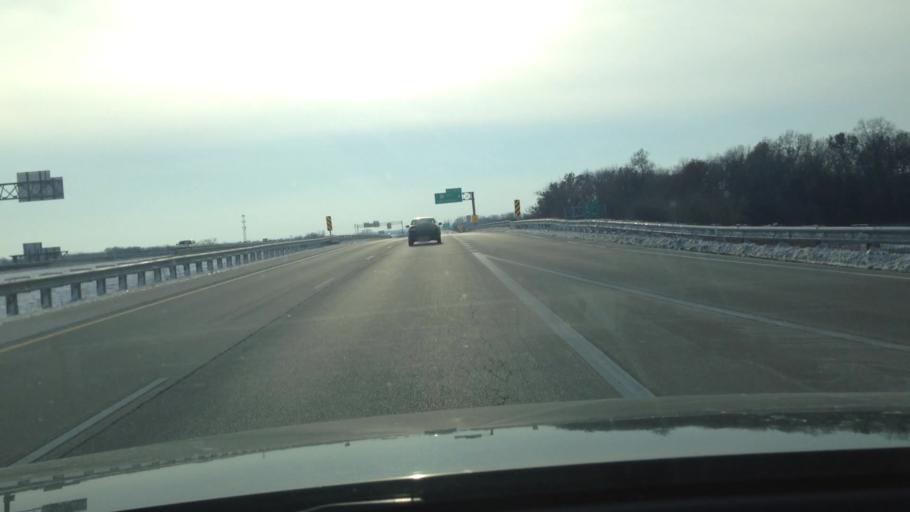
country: US
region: Wisconsin
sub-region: Walworth County
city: Elkhorn
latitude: 42.6756
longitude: -88.5209
